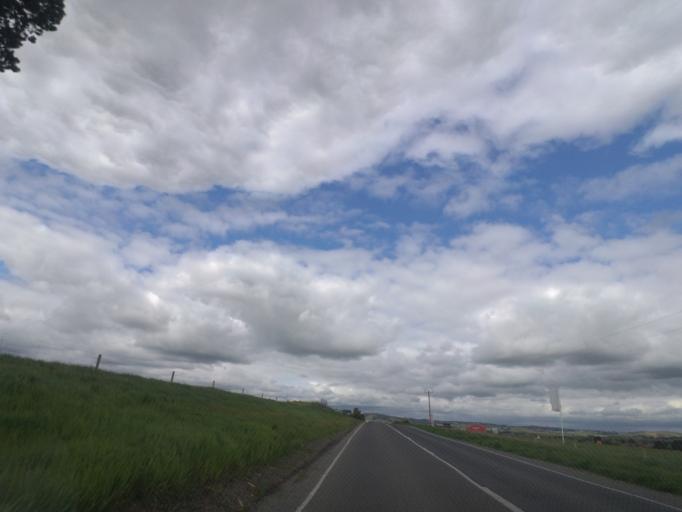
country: AU
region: Victoria
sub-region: Hume
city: Craigieburn
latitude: -37.4698
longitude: 144.9802
